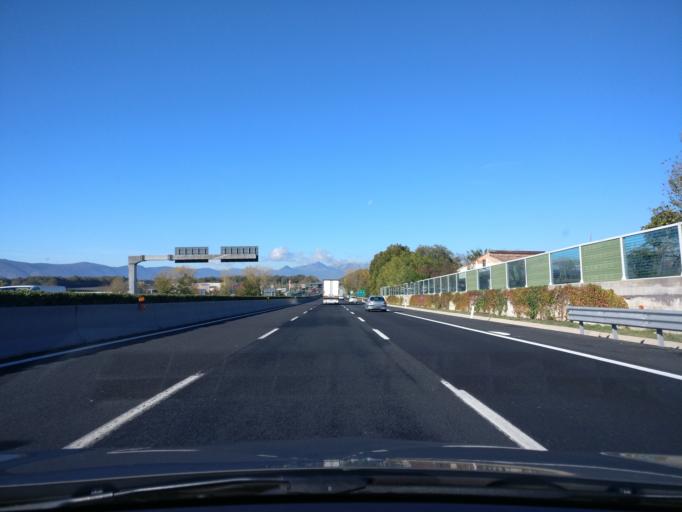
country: IT
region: Latium
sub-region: Provincia di Frosinone
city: Ceprano
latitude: 41.5450
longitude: 13.4864
